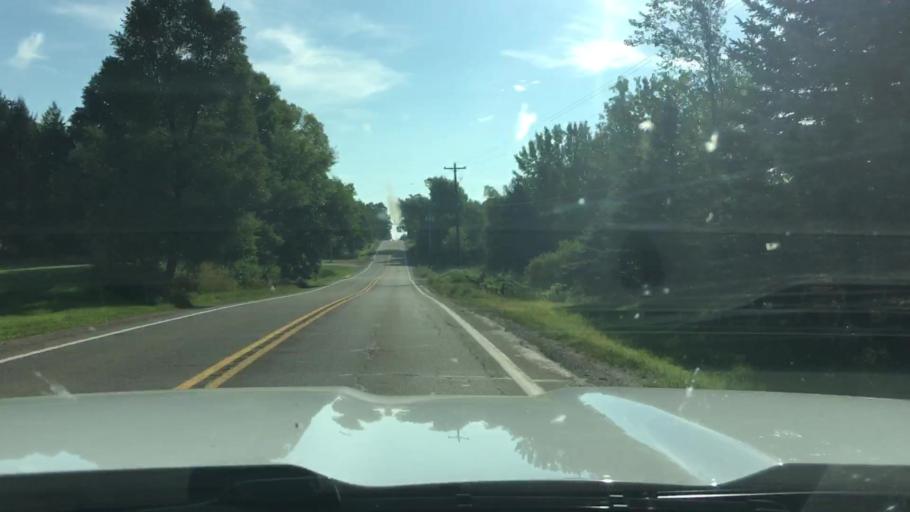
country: US
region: Michigan
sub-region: Kent County
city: Cedar Springs
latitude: 43.2195
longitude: -85.6217
